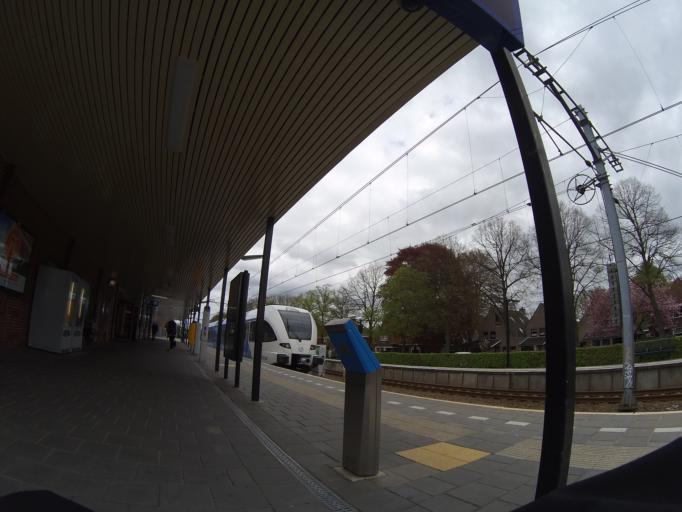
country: NL
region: Drenthe
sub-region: Gemeente Emmen
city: Emmen
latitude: 52.7901
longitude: 6.8995
